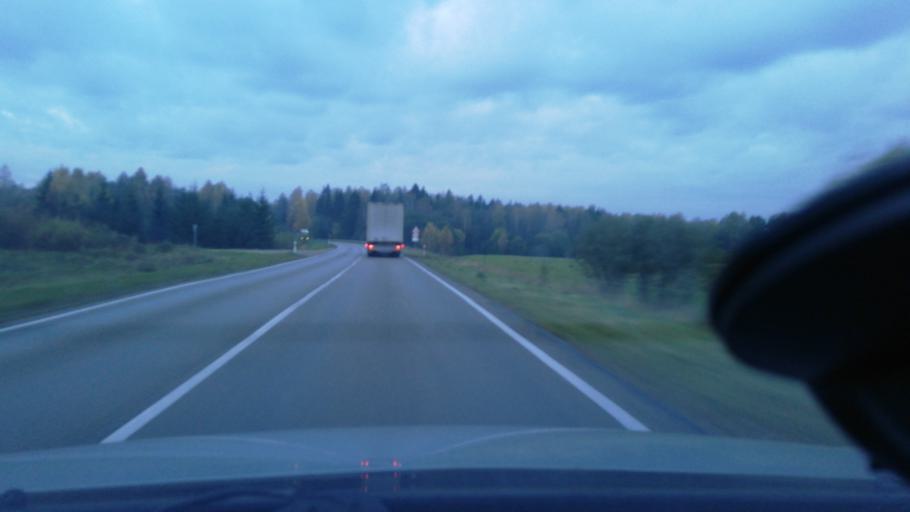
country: LT
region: Klaipedos apskritis
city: Gargzdai
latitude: 55.7655
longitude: 21.5510
